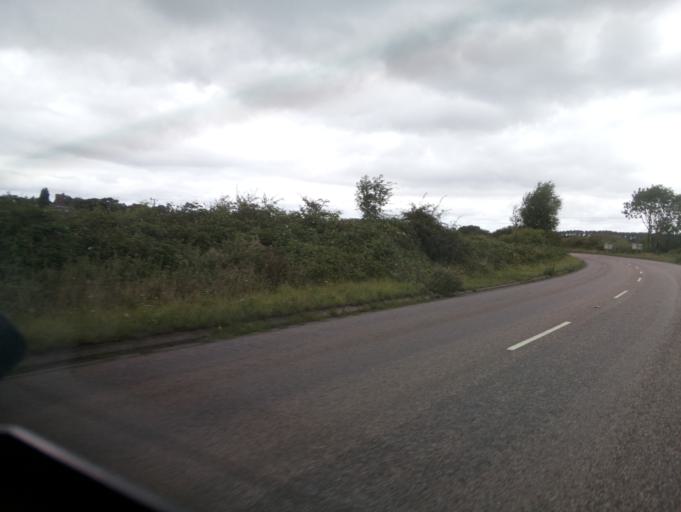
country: GB
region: England
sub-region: Devon
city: Exminster
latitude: 50.6771
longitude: -3.4856
